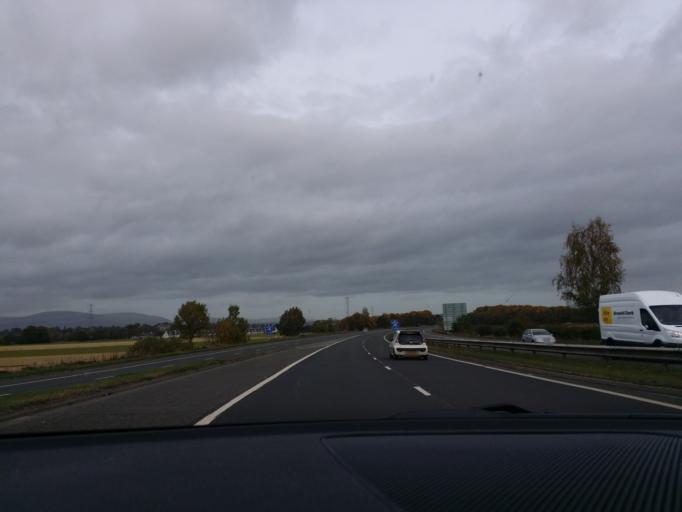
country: GB
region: Scotland
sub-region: Falkirk
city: Airth
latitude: 56.0465
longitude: -3.7799
